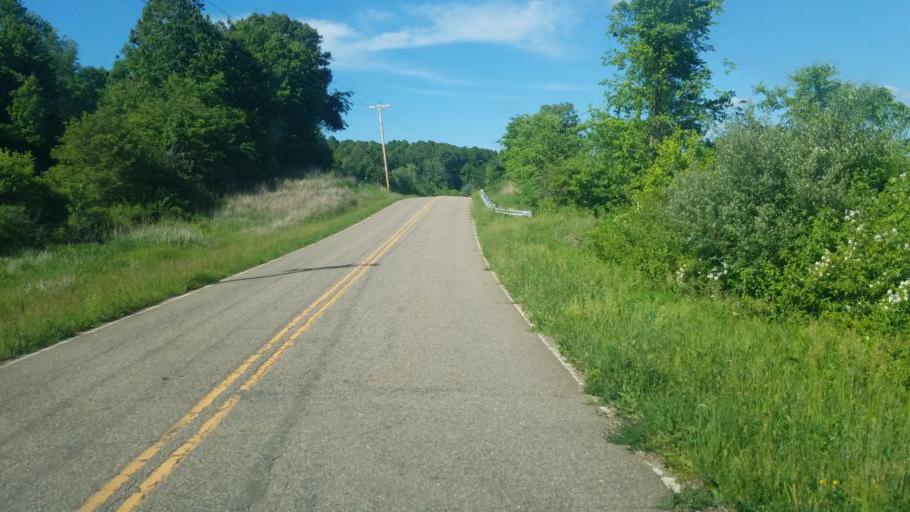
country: US
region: Ohio
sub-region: Guernsey County
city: Mantua
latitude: 40.1757
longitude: -81.6474
